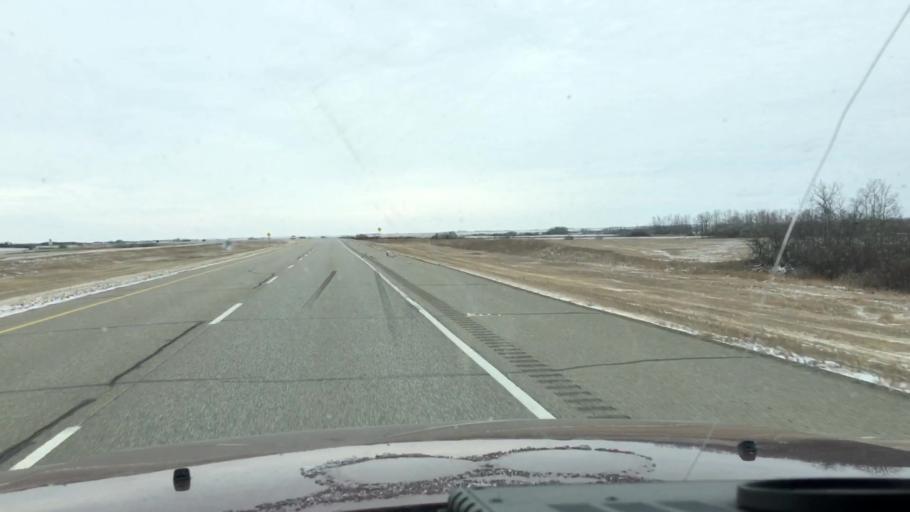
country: CA
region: Saskatchewan
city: Watrous
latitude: 51.3569
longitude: -106.1237
